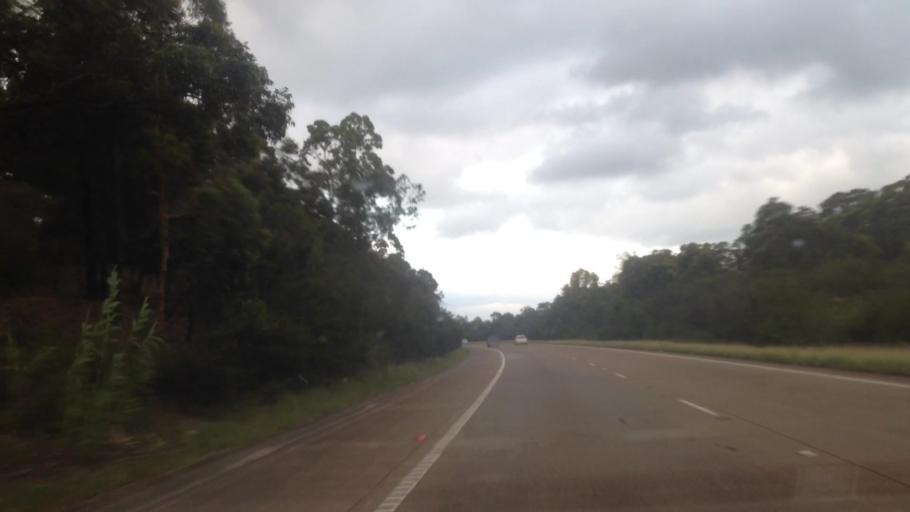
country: AU
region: New South Wales
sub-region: Lake Macquarie Shire
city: Dora Creek
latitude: -33.1462
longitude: 151.4750
